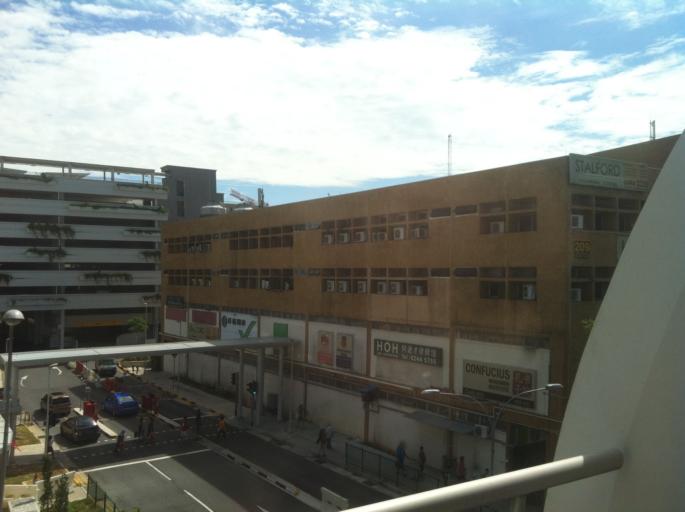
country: SG
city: Singapore
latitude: 1.3243
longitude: 103.9308
